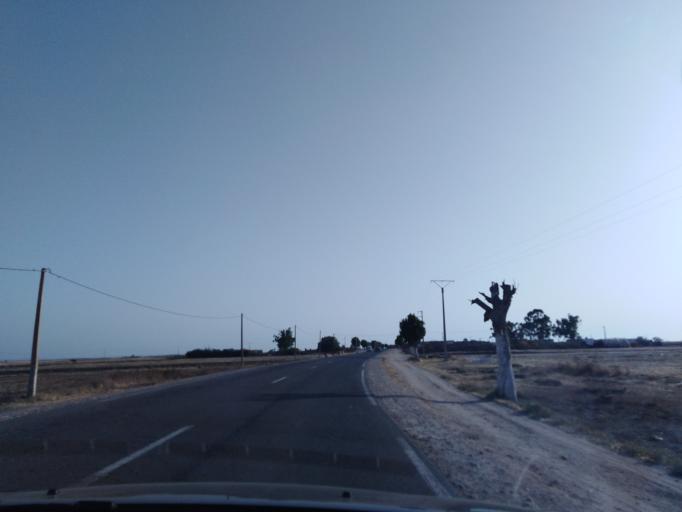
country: MA
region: Doukkala-Abda
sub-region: Safi
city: Youssoufia
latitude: 32.4685
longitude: -8.7748
